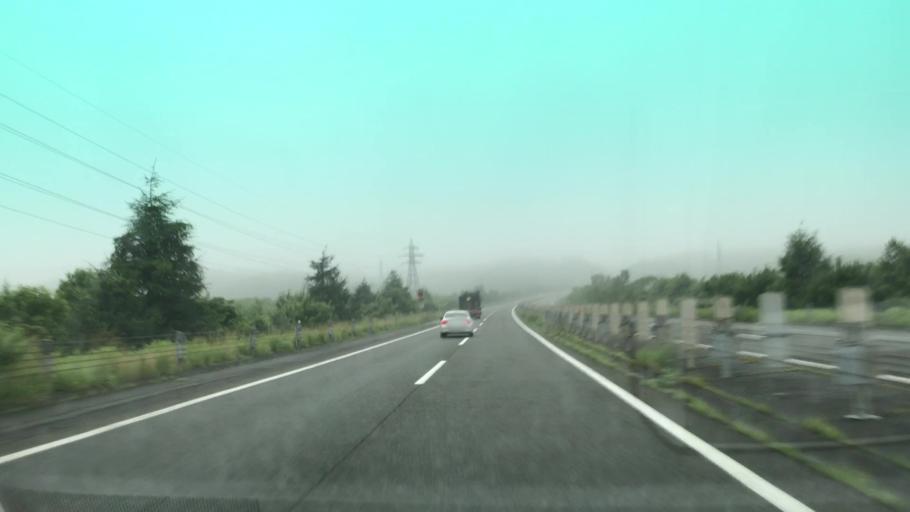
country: JP
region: Hokkaido
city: Tomakomai
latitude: 42.6587
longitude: 141.5766
